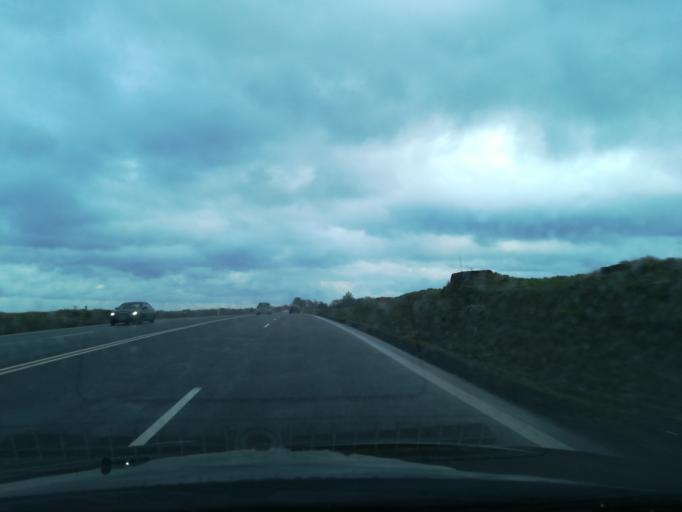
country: PL
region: Subcarpathian Voivodeship
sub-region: Powiat lancucki
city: Gluchow
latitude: 50.0765
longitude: 22.3000
